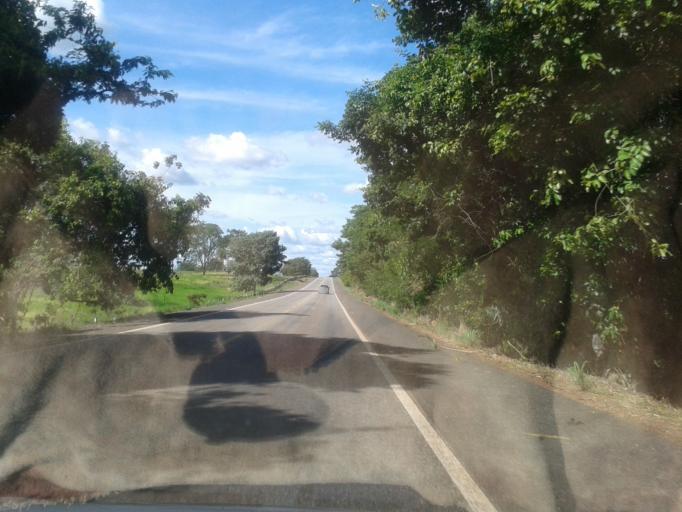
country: BR
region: Goias
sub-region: Mozarlandia
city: Mozarlandia
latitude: -15.0162
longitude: -50.5953
